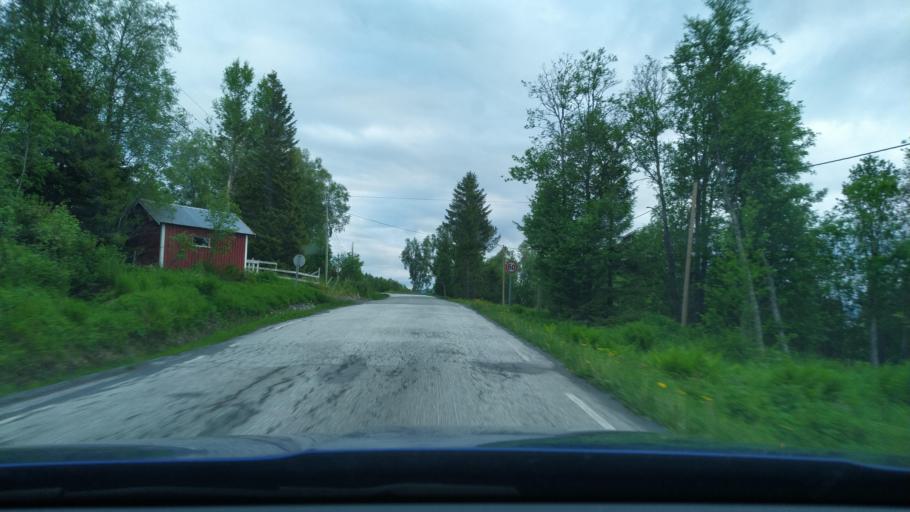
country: NO
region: Troms
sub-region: Tranoy
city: Vangsvika
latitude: 69.1214
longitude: 17.8137
